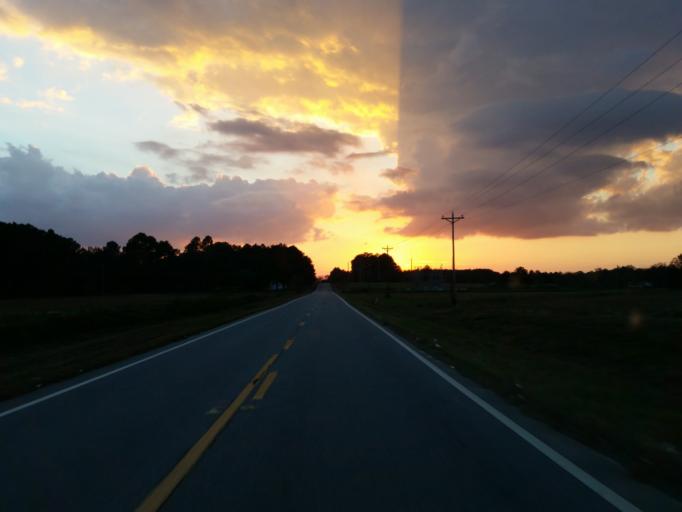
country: US
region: Georgia
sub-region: Dooly County
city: Unadilla
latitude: 32.1617
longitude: -83.6299
